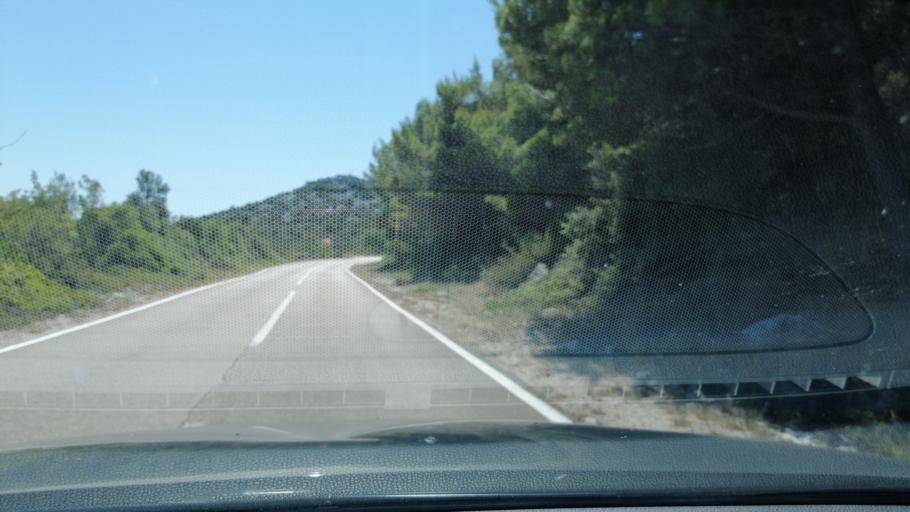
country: HR
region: Sibensko-Kniniska
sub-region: Grad Sibenik
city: Pirovac
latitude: 43.8402
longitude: 15.6896
